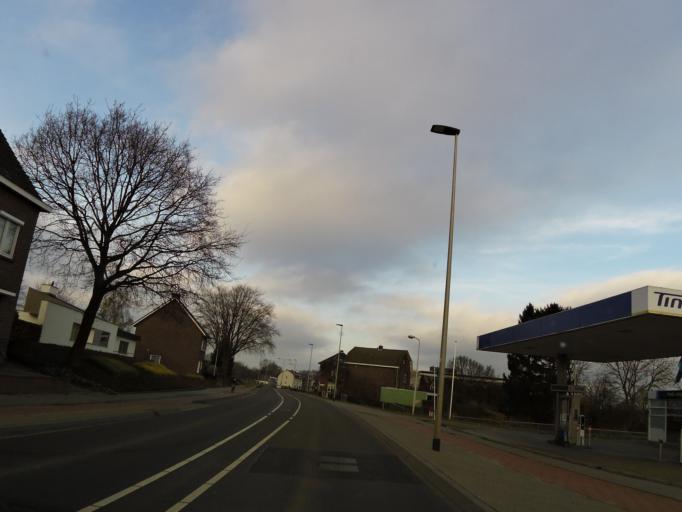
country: NL
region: Limburg
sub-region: Gemeente Nuth
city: Nuth
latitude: 50.9116
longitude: 5.8734
